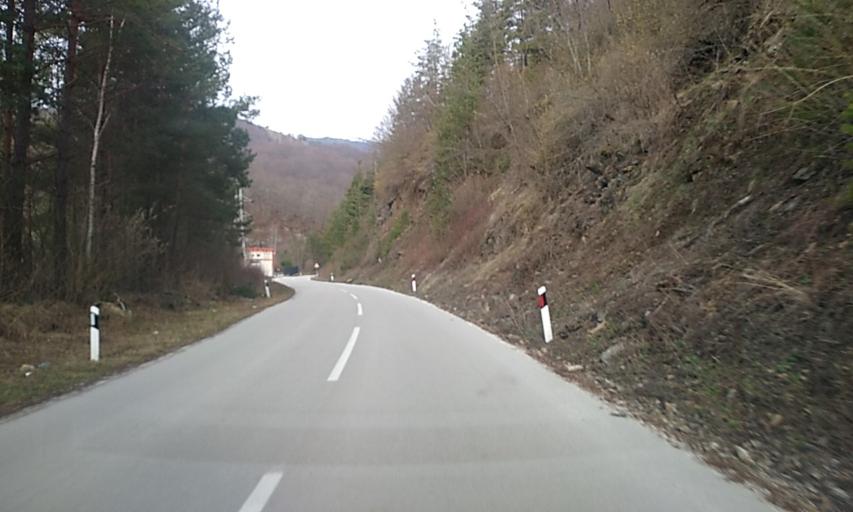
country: RS
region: Central Serbia
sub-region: Pcinjski Okrug
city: Bosilegrad
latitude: 42.5559
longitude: 22.3727
